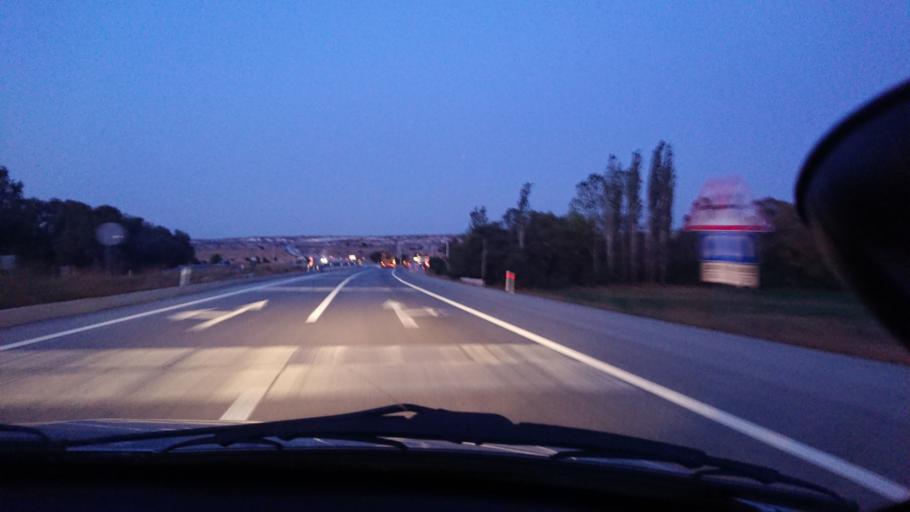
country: TR
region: Kuetahya
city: Cavdarhisar
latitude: 39.1262
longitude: 29.5420
